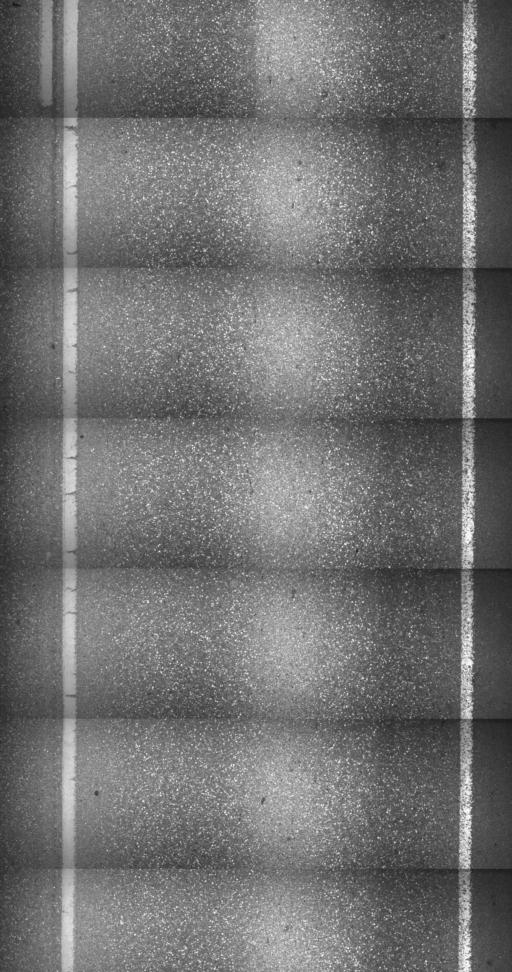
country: US
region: Vermont
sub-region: Chittenden County
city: Hinesburg
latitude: 44.3620
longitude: -73.1246
